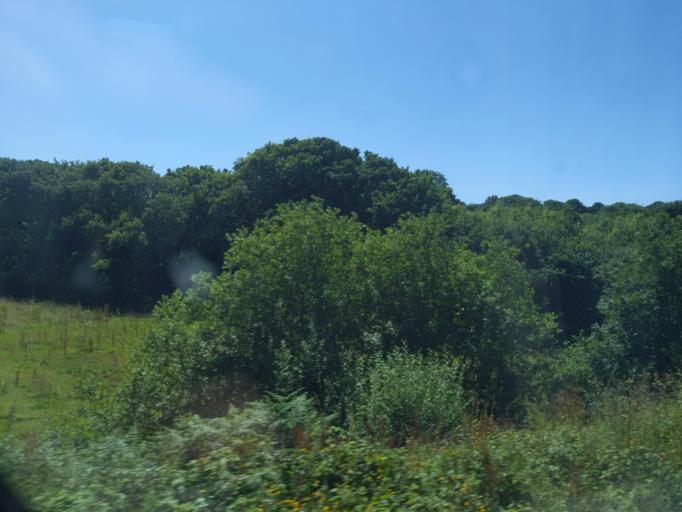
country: GB
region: England
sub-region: Cornwall
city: Saint Stephen
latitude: 50.3278
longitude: -4.8674
